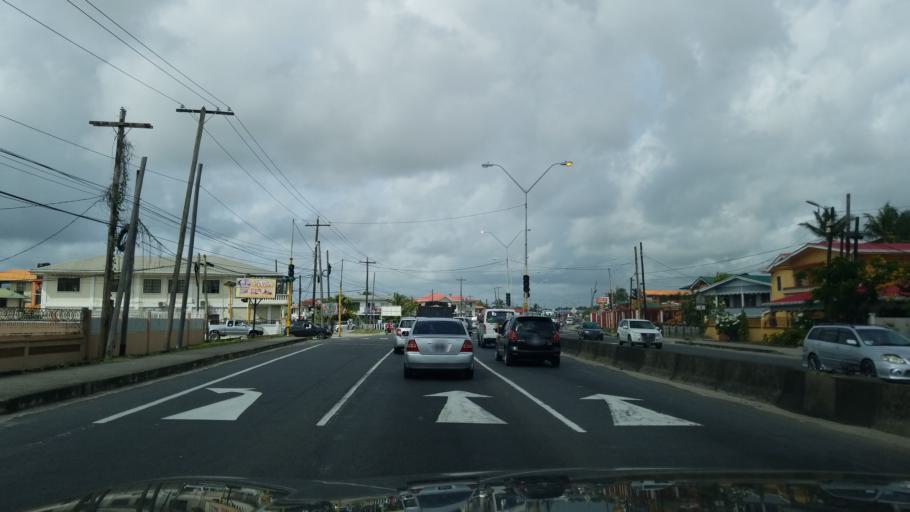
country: GY
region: Demerara-Mahaica
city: Georgetown
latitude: 6.7737
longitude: -58.1727
